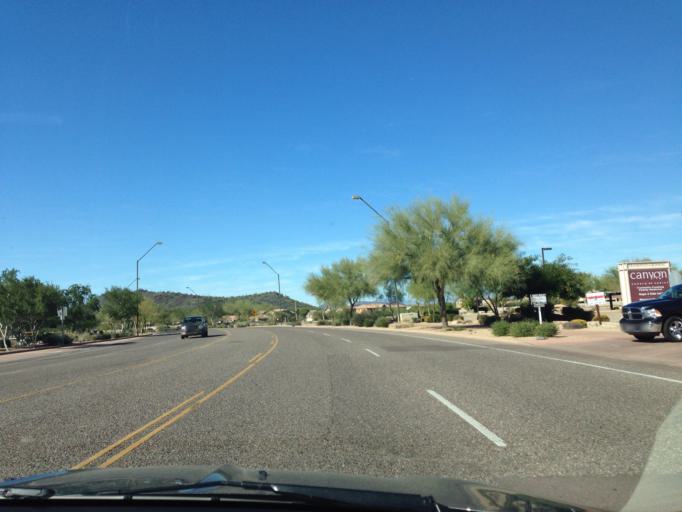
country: US
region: Arizona
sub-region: Maricopa County
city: Anthem
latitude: 33.8014
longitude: -112.1299
